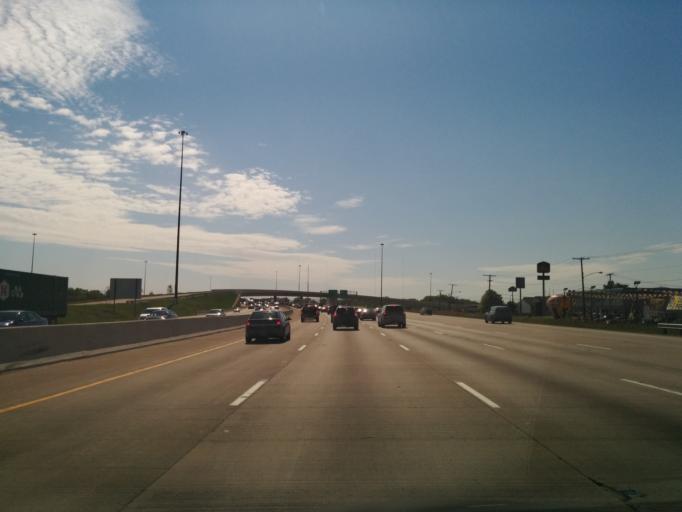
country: US
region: Indiana
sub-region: Lake County
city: Highland
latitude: 41.5713
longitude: -87.4388
